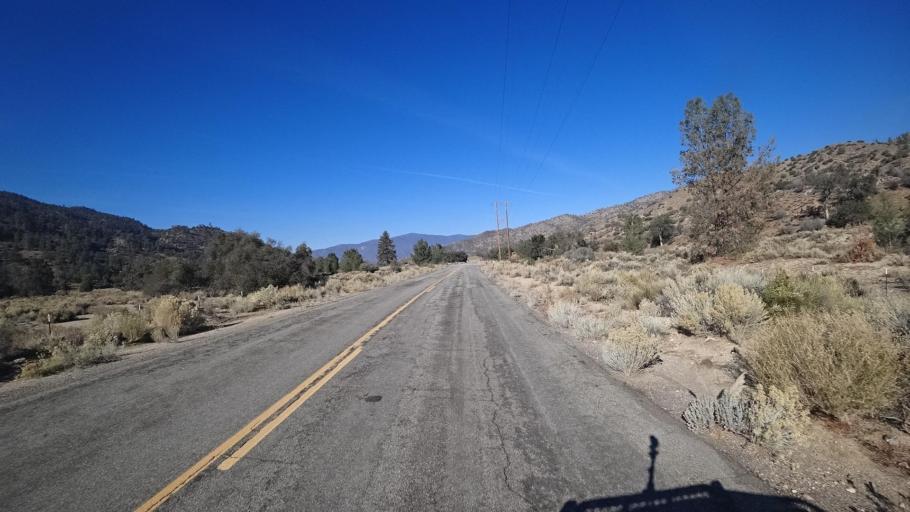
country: US
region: California
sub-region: Kern County
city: Bodfish
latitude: 35.3895
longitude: -118.4281
